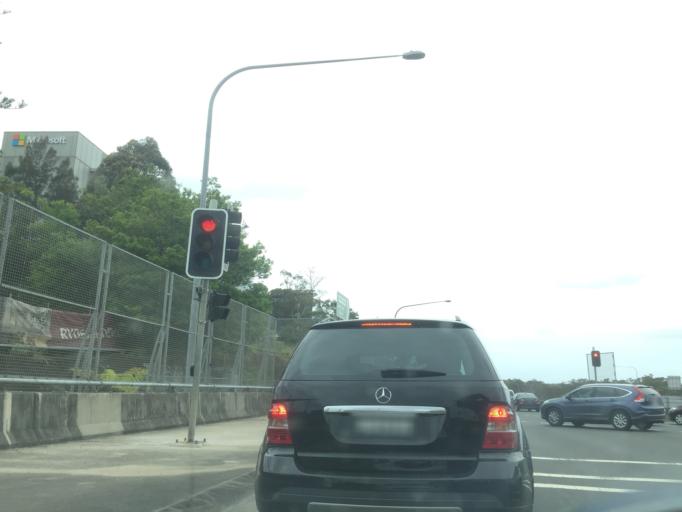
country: AU
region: New South Wales
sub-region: Ryde
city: North Ryde
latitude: -33.7962
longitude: 151.1370
